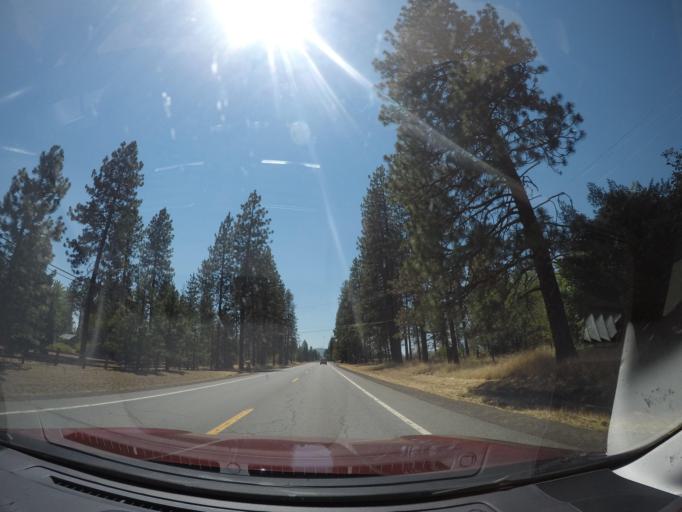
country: US
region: California
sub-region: Shasta County
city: Burney
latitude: 41.0606
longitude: -121.3704
